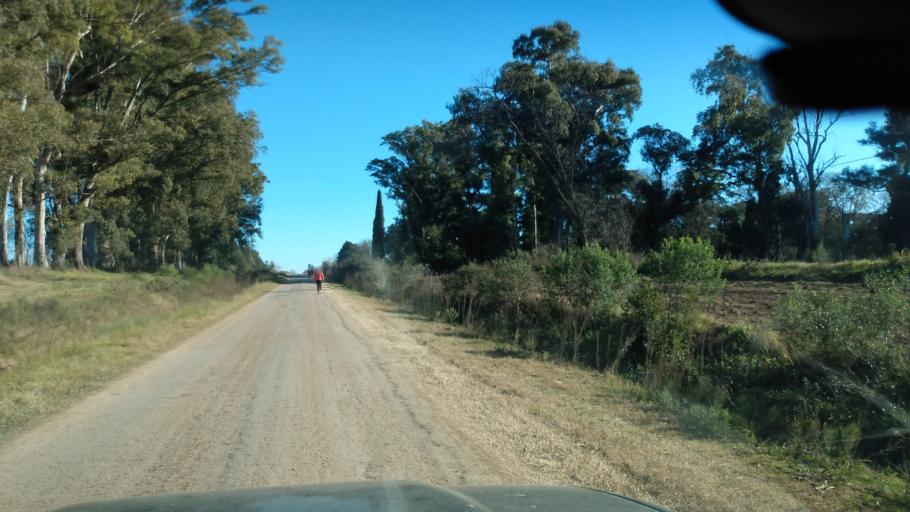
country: AR
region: Buenos Aires
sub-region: Partido de Lujan
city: Lujan
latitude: -34.5655
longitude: -59.1706
